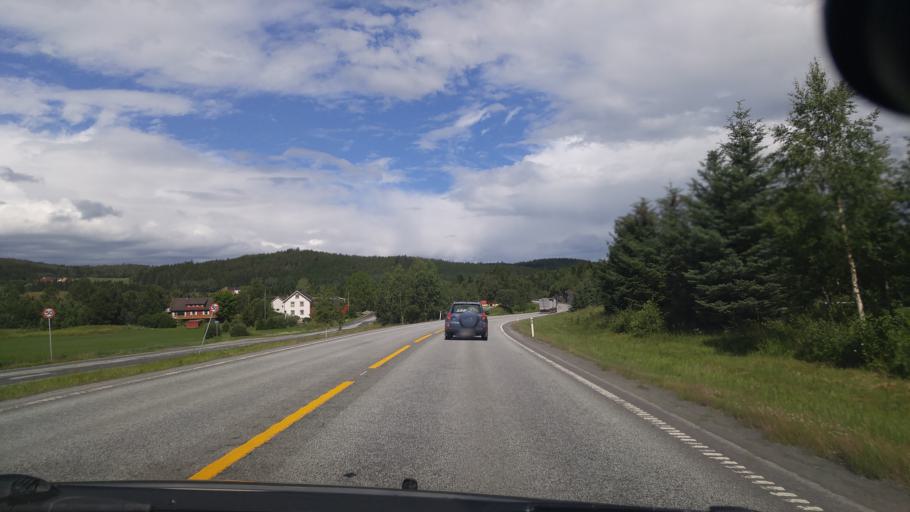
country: NO
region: Nord-Trondelag
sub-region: Levanger
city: Skogn
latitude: 63.6300
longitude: 11.0665
